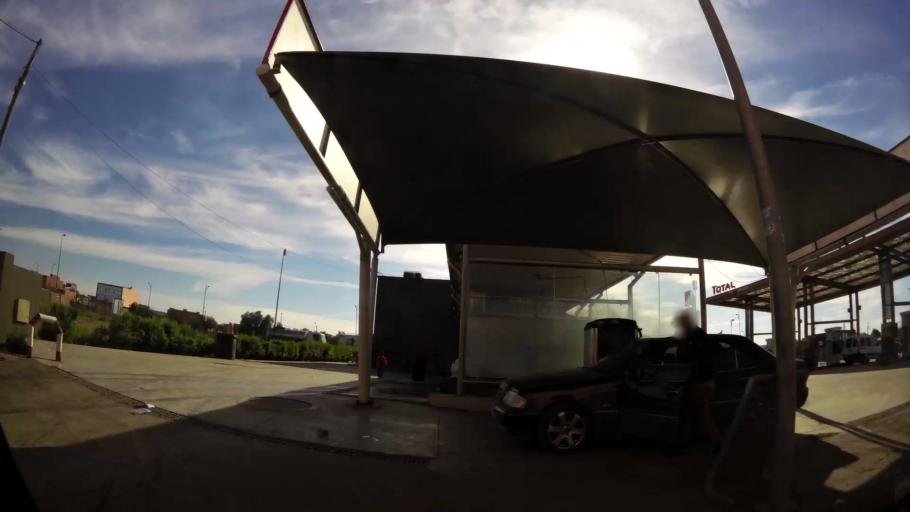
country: MA
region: Marrakech-Tensift-Al Haouz
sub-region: Marrakech
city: Marrakesh
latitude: 31.6810
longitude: -8.0482
